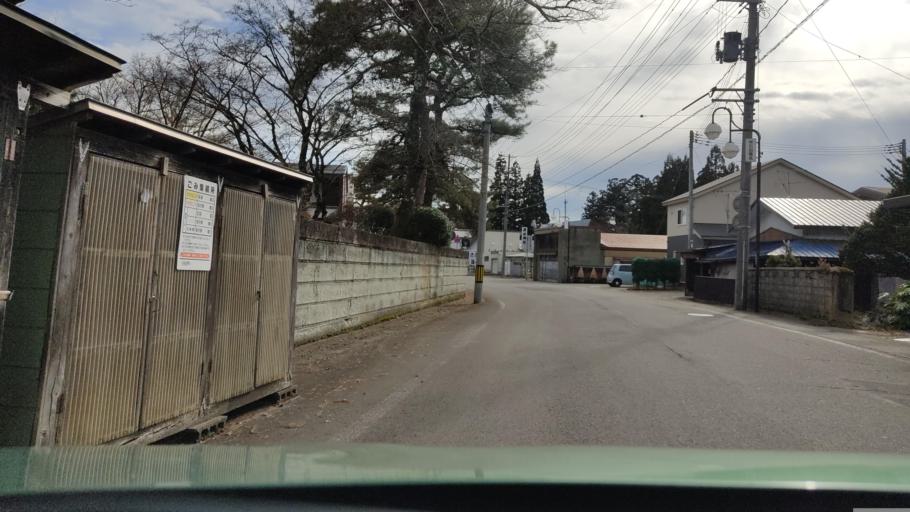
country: JP
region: Akita
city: Omagari
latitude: 39.6131
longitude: 140.3221
